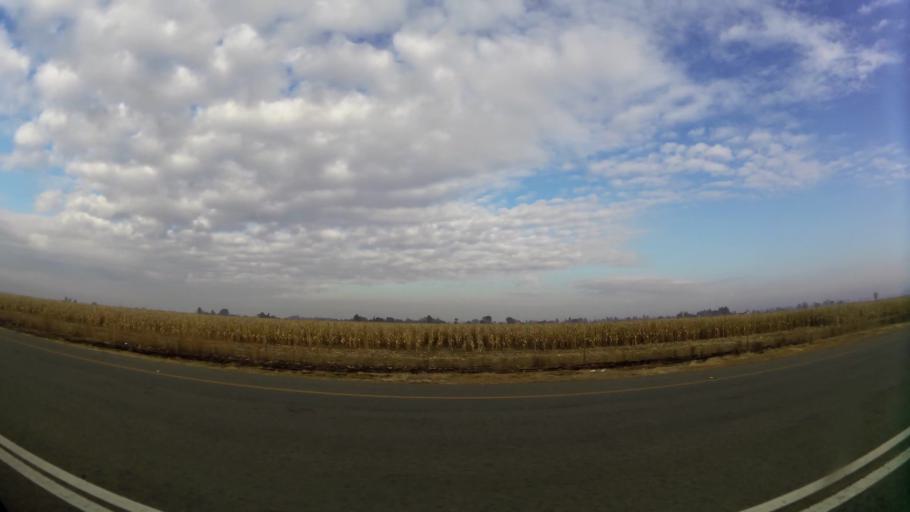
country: ZA
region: Gauteng
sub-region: Sedibeng District Municipality
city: Vanderbijlpark
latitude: -26.6375
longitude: 27.7744
